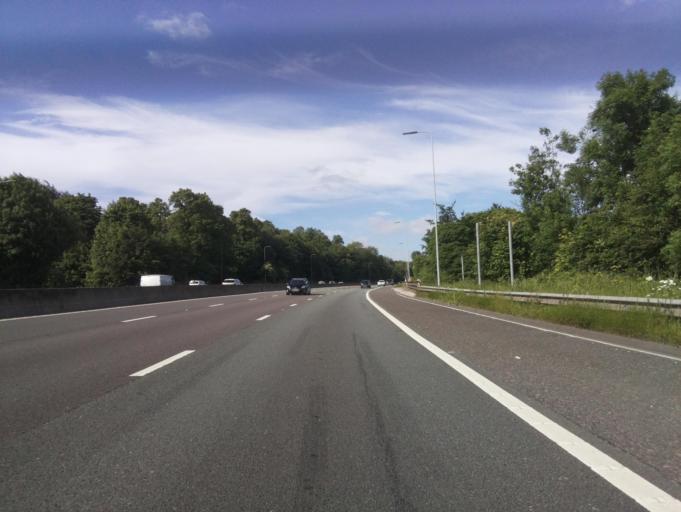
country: GB
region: England
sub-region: City and Borough of Salford
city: Walkden
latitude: 53.5005
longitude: -2.3837
